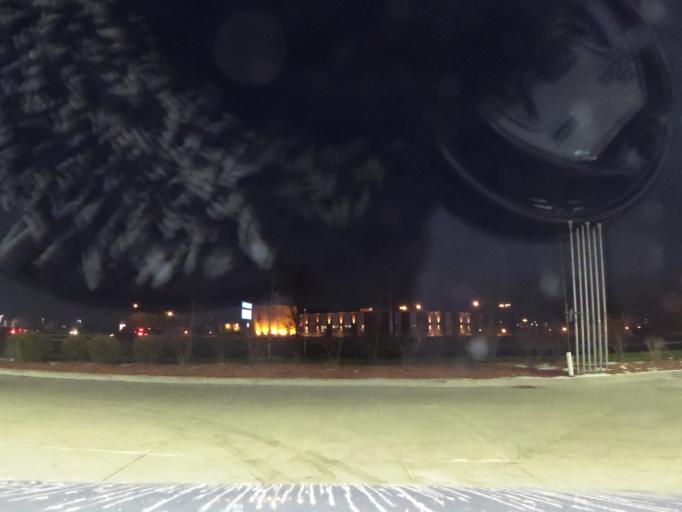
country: US
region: Indiana
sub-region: Lake County
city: Crown Point
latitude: 41.4195
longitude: -87.3360
